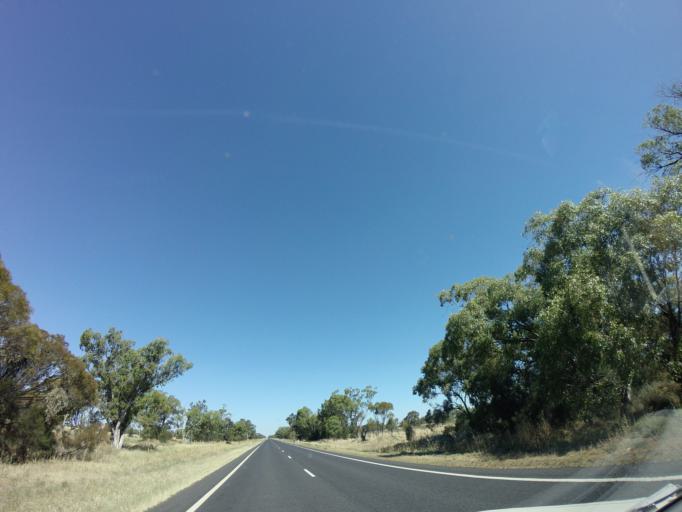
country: AU
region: New South Wales
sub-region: Bogan
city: Nyngan
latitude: -31.7842
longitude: 147.6158
